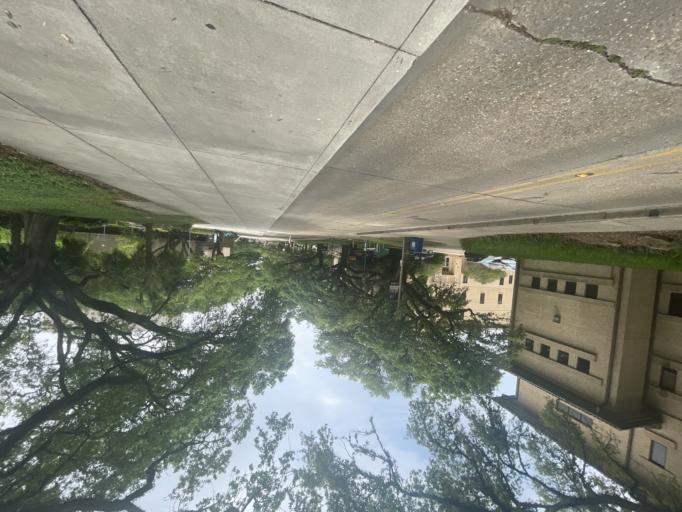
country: US
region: Louisiana
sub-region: East Baton Rouge Parish
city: Baton Rouge
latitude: 30.4119
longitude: -91.1782
